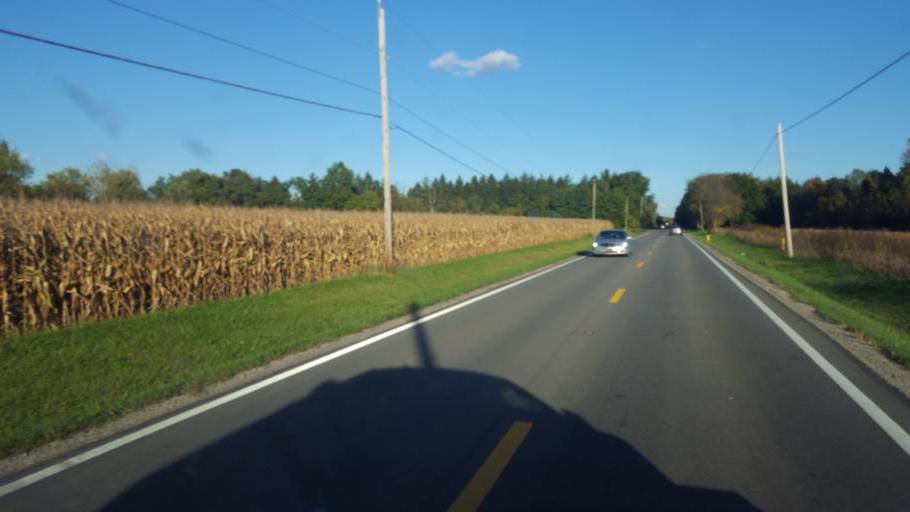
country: US
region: Ohio
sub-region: Franklin County
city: New Albany
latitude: 40.0189
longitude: -82.7825
